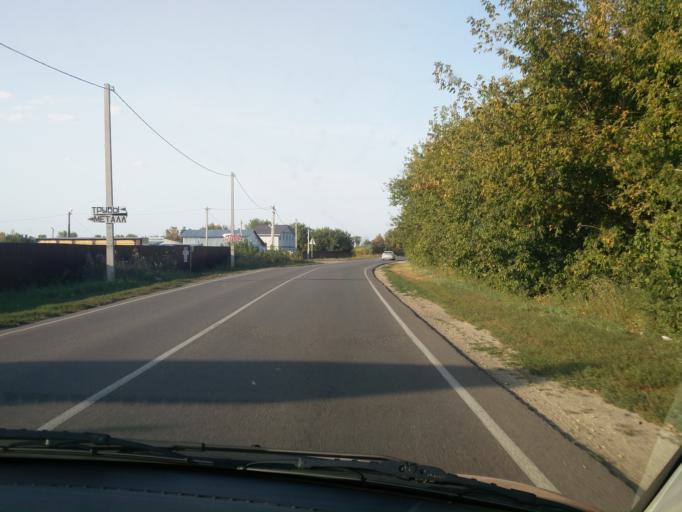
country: RU
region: Voronezj
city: Ramon'
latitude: 51.9184
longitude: 39.3205
